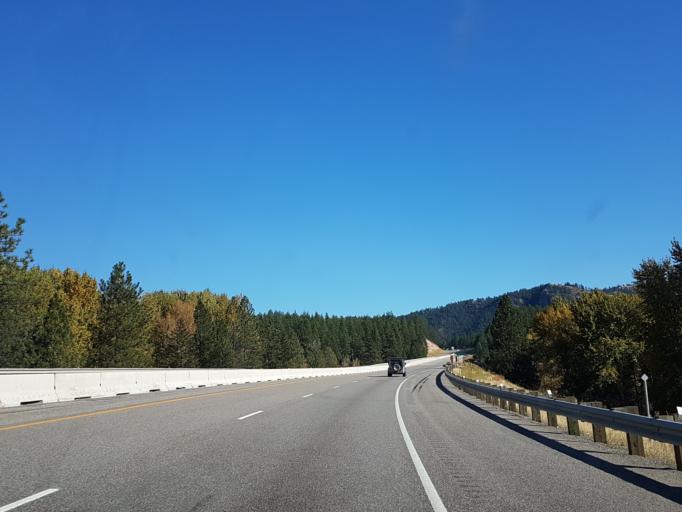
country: US
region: Montana
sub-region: Missoula County
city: Frenchtown
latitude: 47.0231
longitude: -114.3870
